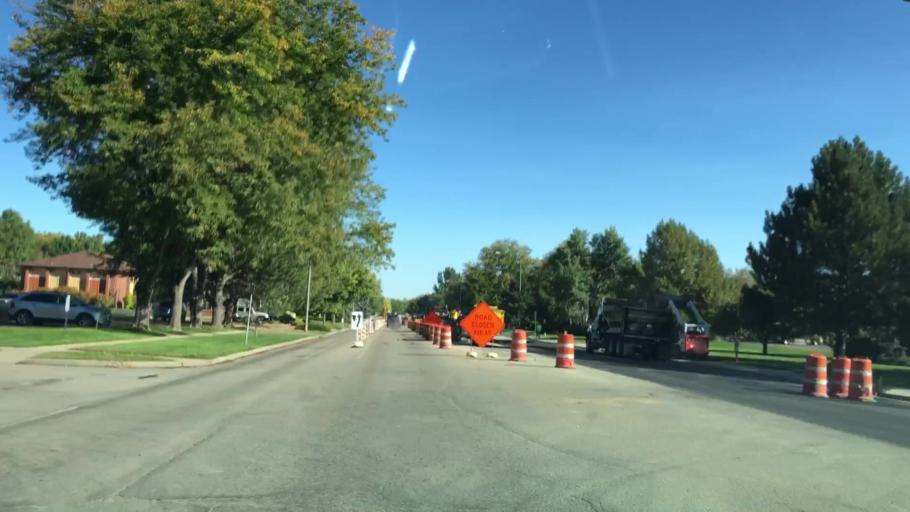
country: US
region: Colorado
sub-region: Larimer County
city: Loveland
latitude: 40.4125
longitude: -105.0537
